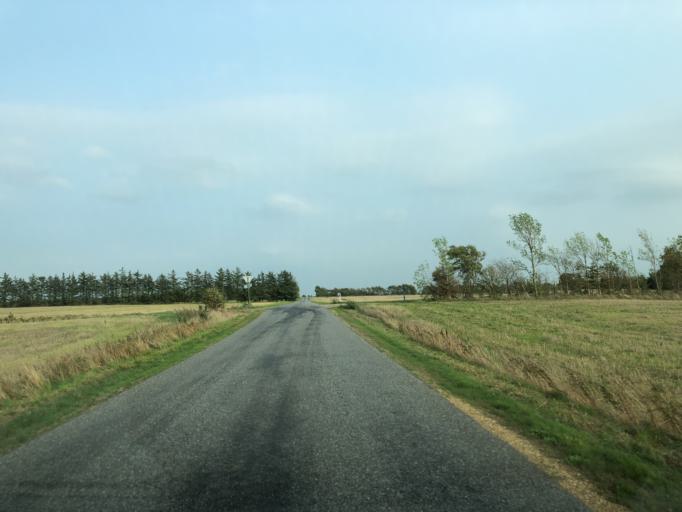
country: DK
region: Central Jutland
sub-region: Ringkobing-Skjern Kommune
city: Videbaek
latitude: 56.1233
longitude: 8.6526
